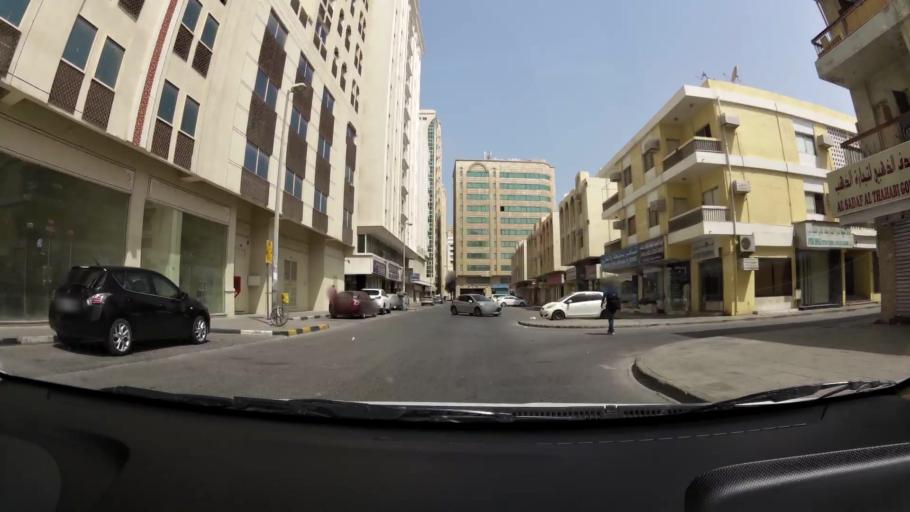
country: AE
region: Ash Shariqah
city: Sharjah
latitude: 25.3545
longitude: 55.3835
